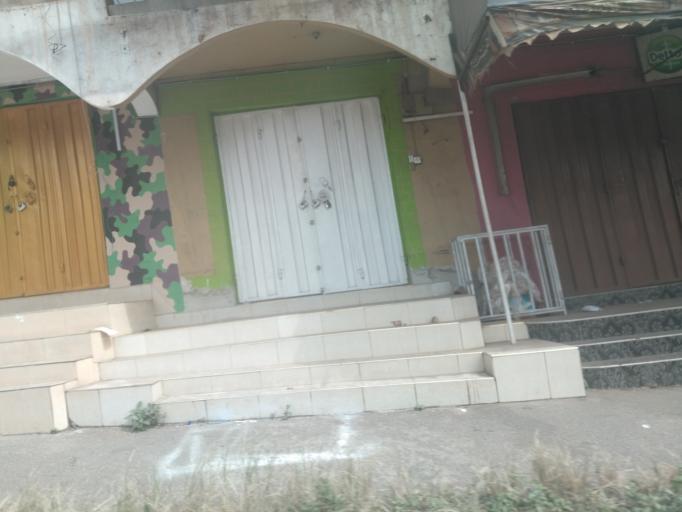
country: GH
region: Ashanti
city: Kumasi
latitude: 6.7105
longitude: -1.6166
